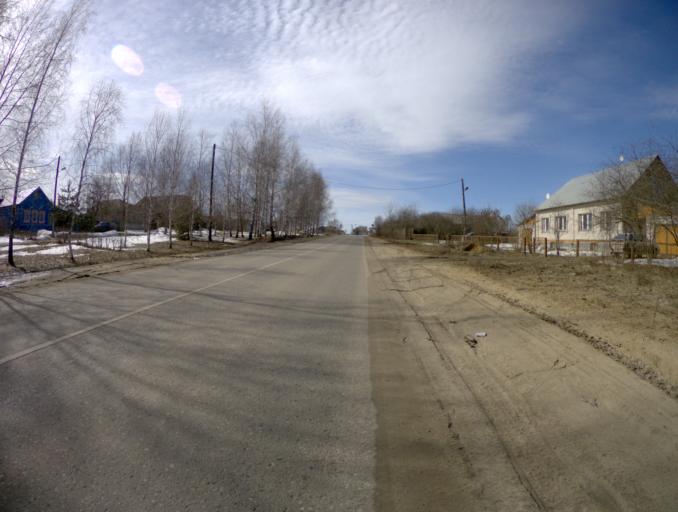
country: RU
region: Vladimir
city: Suzdal'
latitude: 56.4277
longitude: 40.4194
